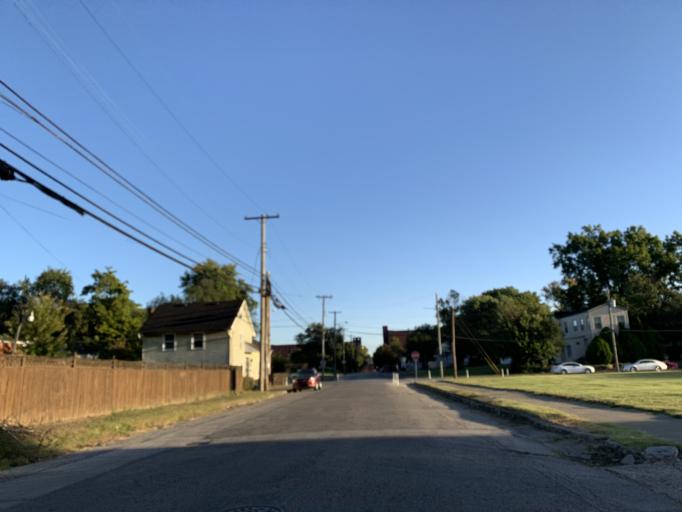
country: US
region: Kentucky
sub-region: Jefferson County
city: Louisville
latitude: 38.2410
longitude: -85.7803
